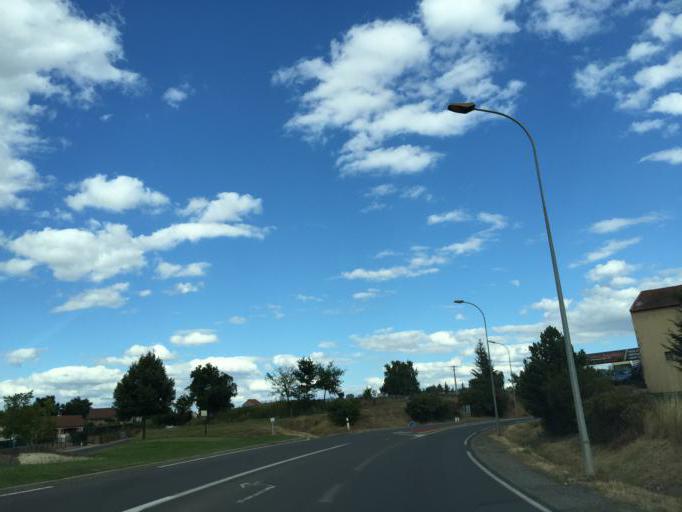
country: FR
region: Rhone-Alpes
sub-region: Departement de la Loire
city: Savigneux
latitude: 45.6126
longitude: 4.0833
